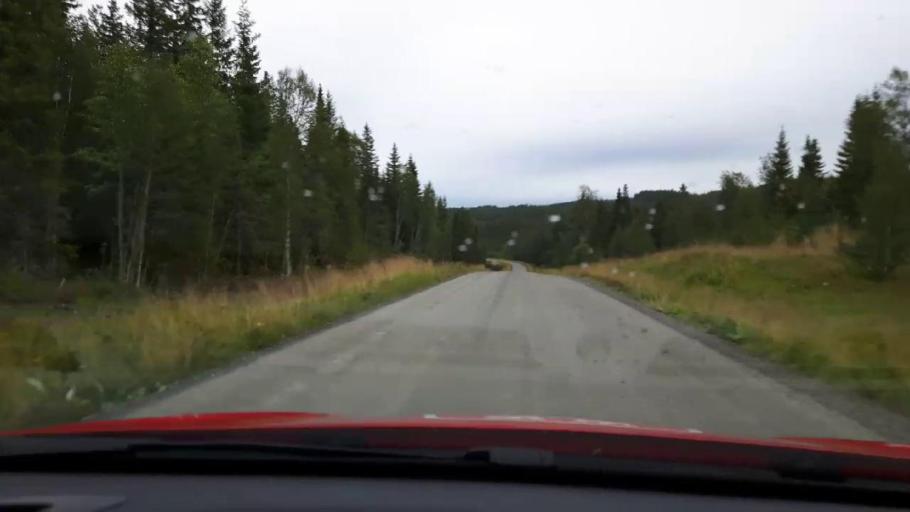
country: SE
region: Jaemtland
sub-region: Are Kommun
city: Are
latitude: 63.4318
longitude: 13.2876
